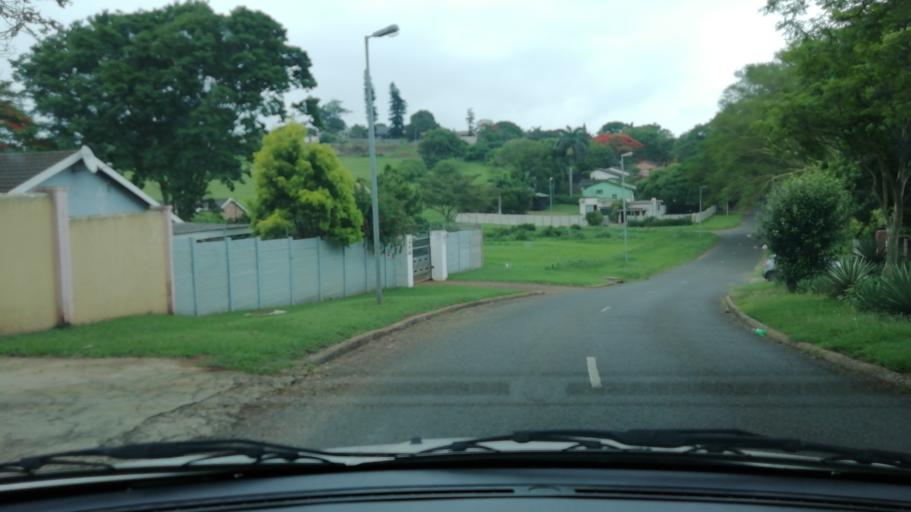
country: ZA
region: KwaZulu-Natal
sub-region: uThungulu District Municipality
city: Empangeni
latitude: -28.7398
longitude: 31.9025
